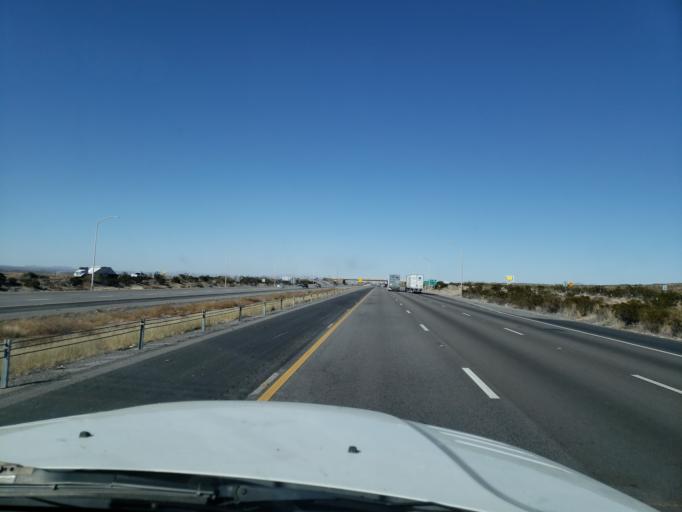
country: US
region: New Mexico
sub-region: Dona Ana County
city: Mesquite
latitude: 32.1691
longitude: -106.6661
